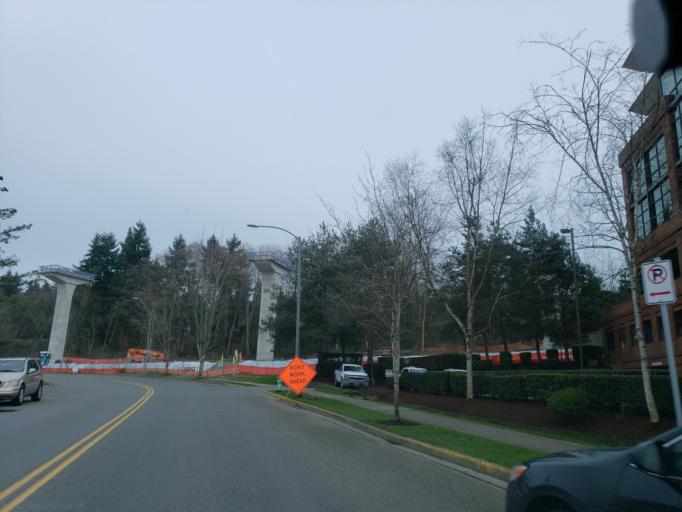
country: US
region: Washington
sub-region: Snohomish County
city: Mountlake Terrace
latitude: 47.8008
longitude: -122.3168
